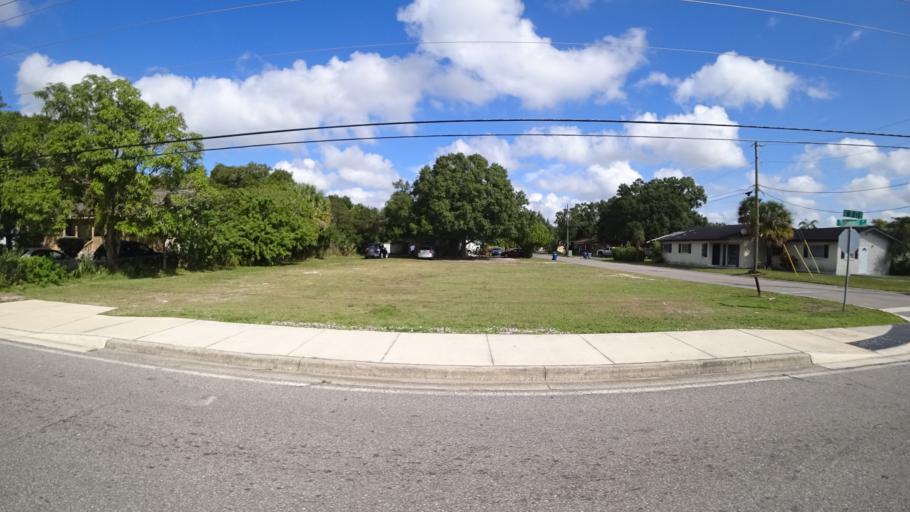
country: US
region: Florida
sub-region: Manatee County
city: Whitfield
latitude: 27.4036
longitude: -82.5450
